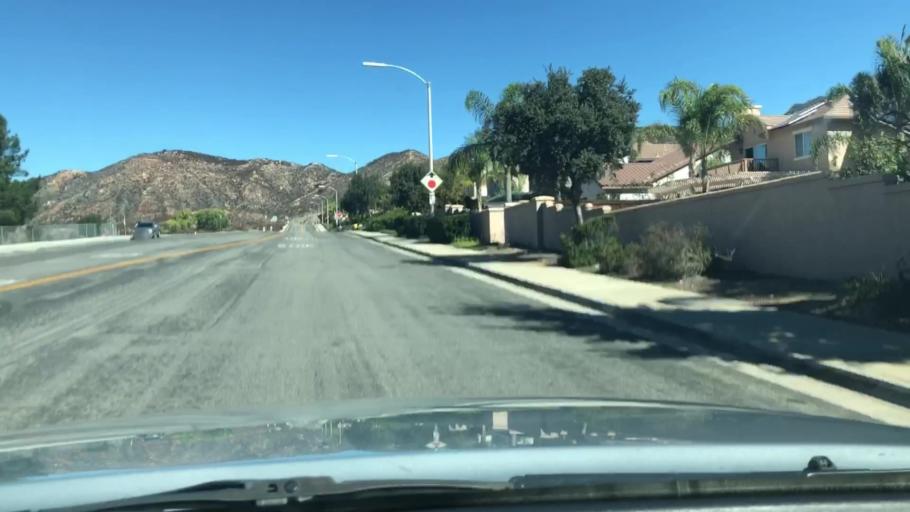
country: US
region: California
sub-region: Riverside County
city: Wildomar
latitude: 33.6060
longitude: -117.2408
